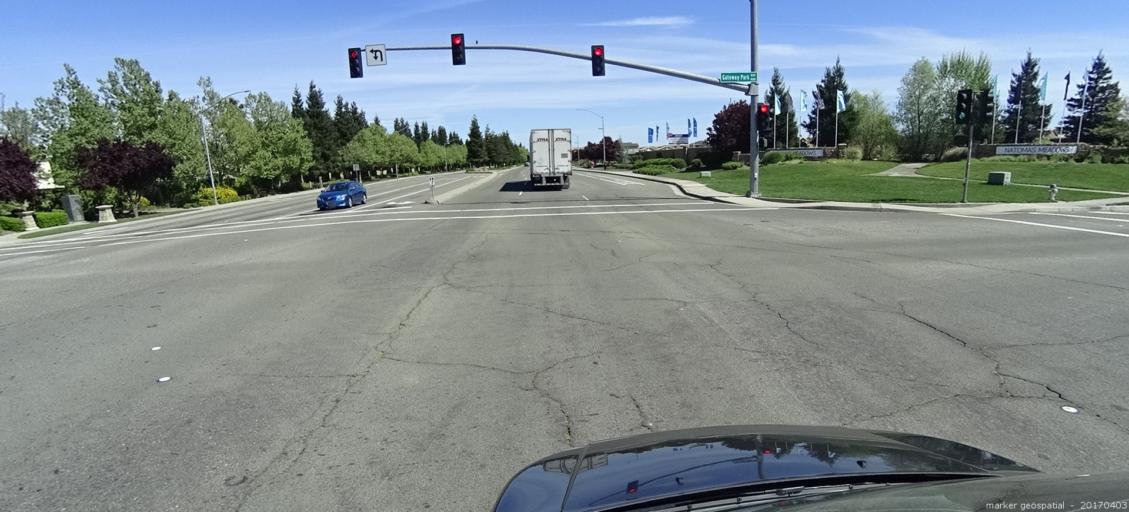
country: US
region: California
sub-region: Sacramento County
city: Rio Linda
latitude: 38.6561
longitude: -121.5029
